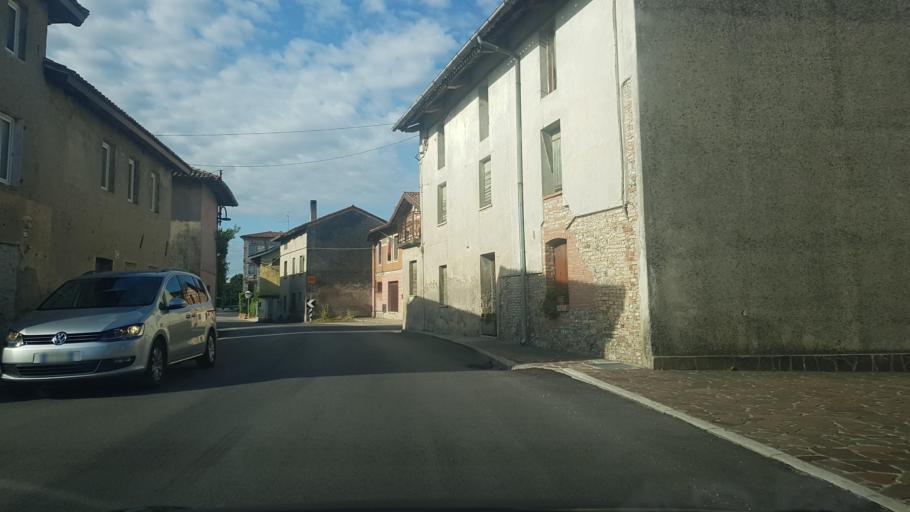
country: IT
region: Friuli Venezia Giulia
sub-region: Provincia di Udine
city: Porpetto
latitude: 45.8717
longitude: 13.2226
